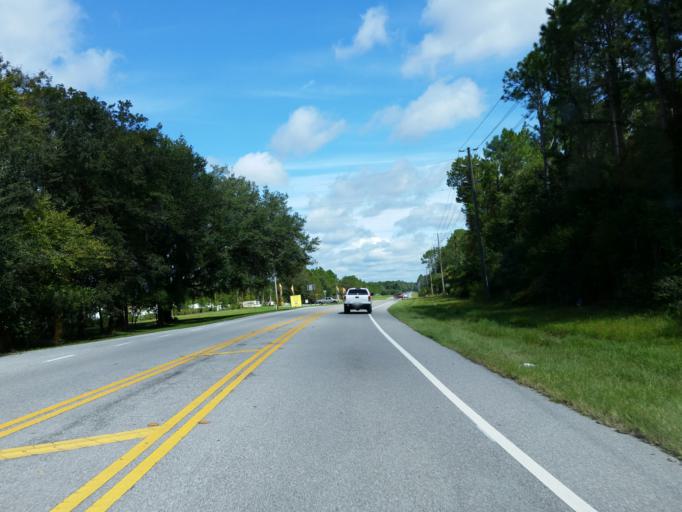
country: US
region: Florida
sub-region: Pasco County
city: Land O' Lakes
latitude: 28.2012
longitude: -82.3984
